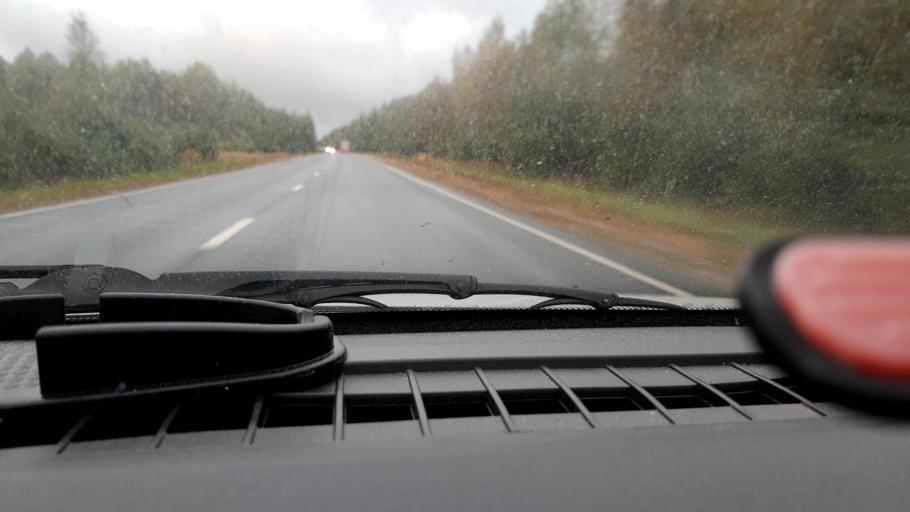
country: RU
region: Nizjnij Novgorod
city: Semenov
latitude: 56.7845
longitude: 44.4403
